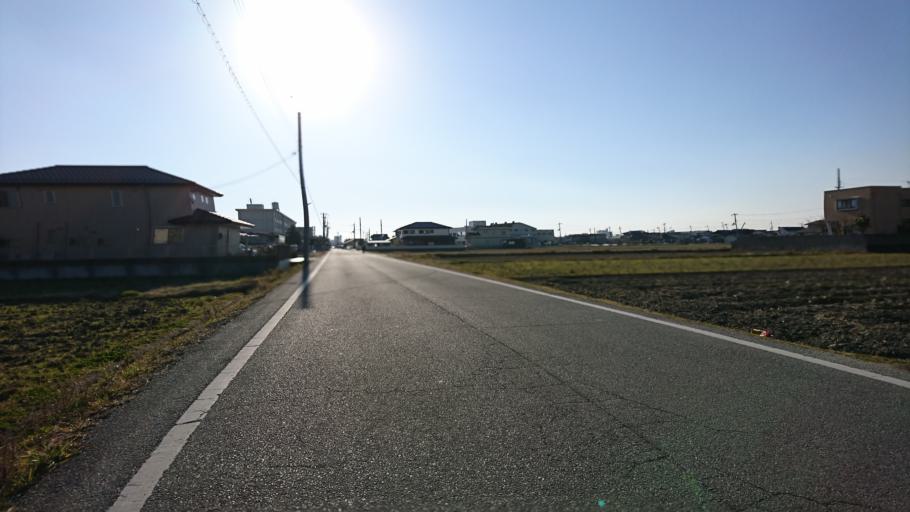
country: JP
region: Hyogo
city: Kakogawacho-honmachi
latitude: 34.7724
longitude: 134.8585
